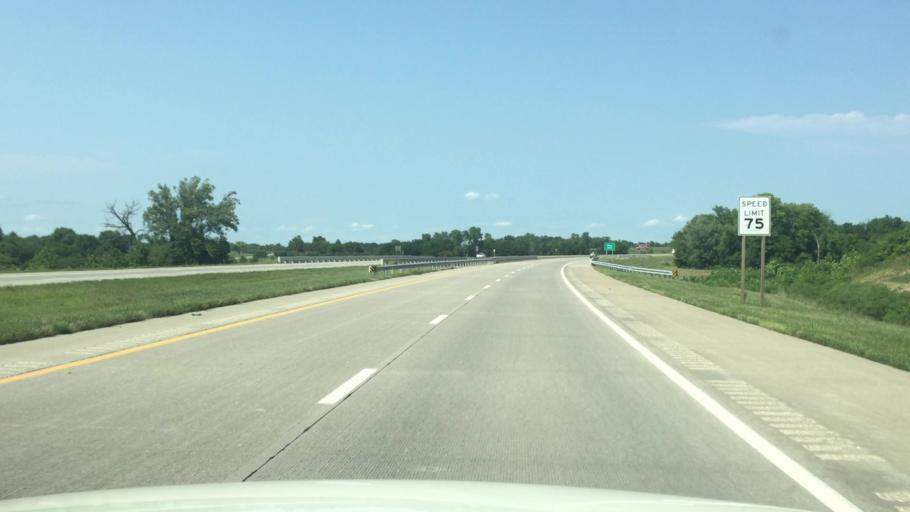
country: US
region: Kansas
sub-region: Linn County
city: Pleasanton
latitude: 38.1368
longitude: -94.7130
